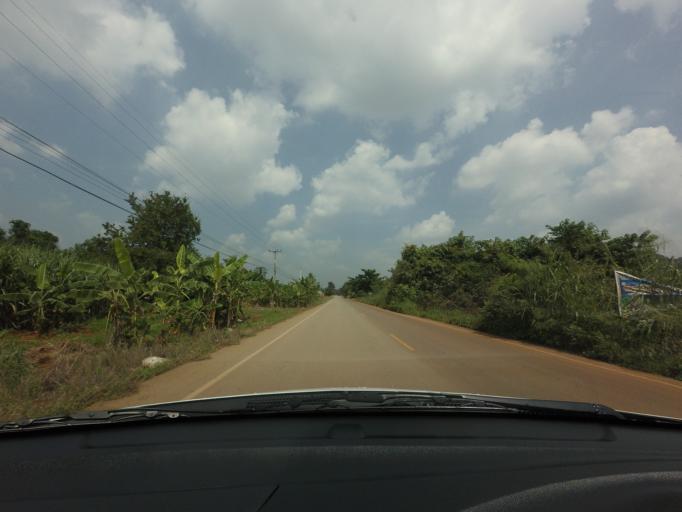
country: TH
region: Nakhon Ratchasima
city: Pak Chong
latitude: 14.5600
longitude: 101.5723
